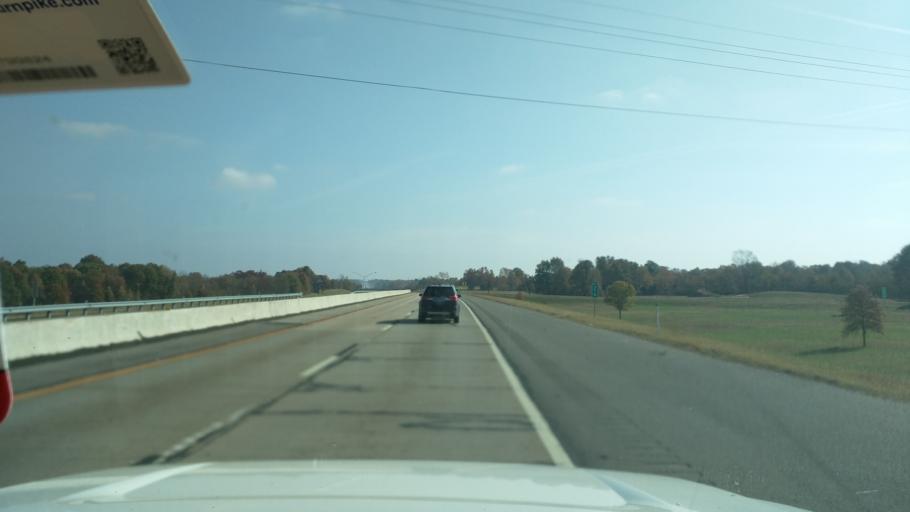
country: US
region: Oklahoma
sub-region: Muskogee County
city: Muskogee
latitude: 35.8439
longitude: -95.4025
